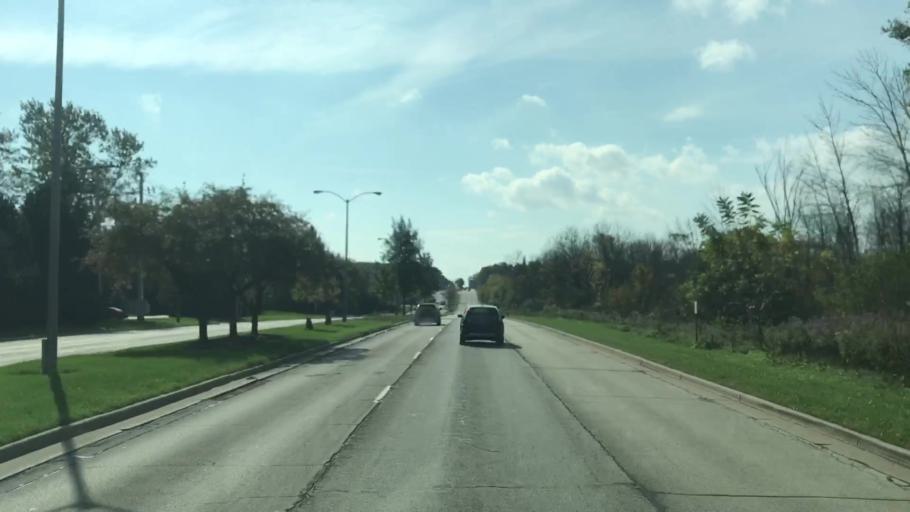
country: US
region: Wisconsin
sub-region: Waukesha County
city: Butler
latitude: 43.1613
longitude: -88.0447
